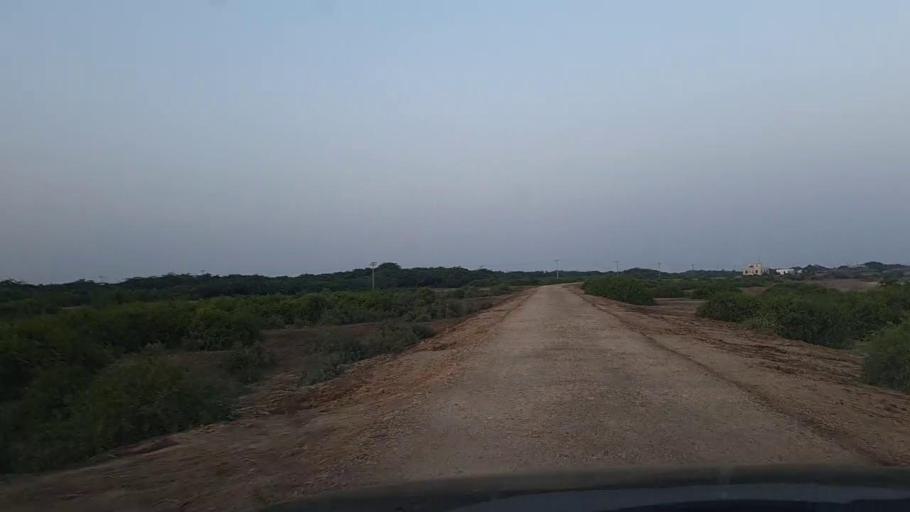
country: PK
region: Sindh
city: Mirpur Sakro
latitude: 24.6376
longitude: 67.6617
